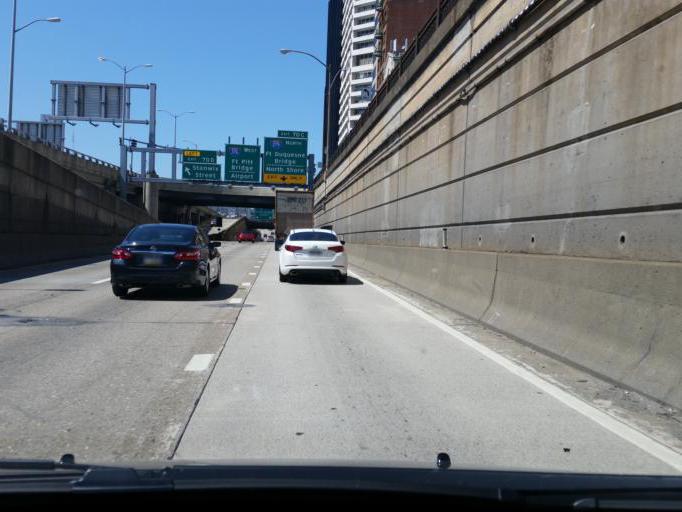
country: US
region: Pennsylvania
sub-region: Allegheny County
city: Pittsburgh
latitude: 40.4375
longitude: -80.0039
